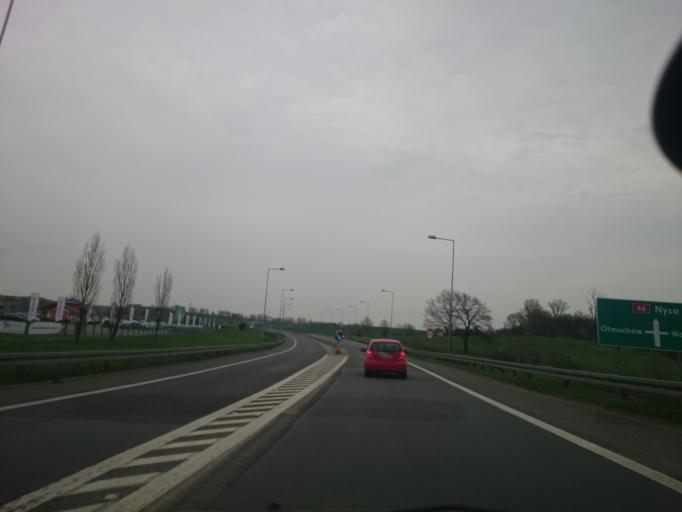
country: PL
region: Opole Voivodeship
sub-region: Powiat nyski
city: Otmuchow
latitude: 50.4592
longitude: 17.1938
